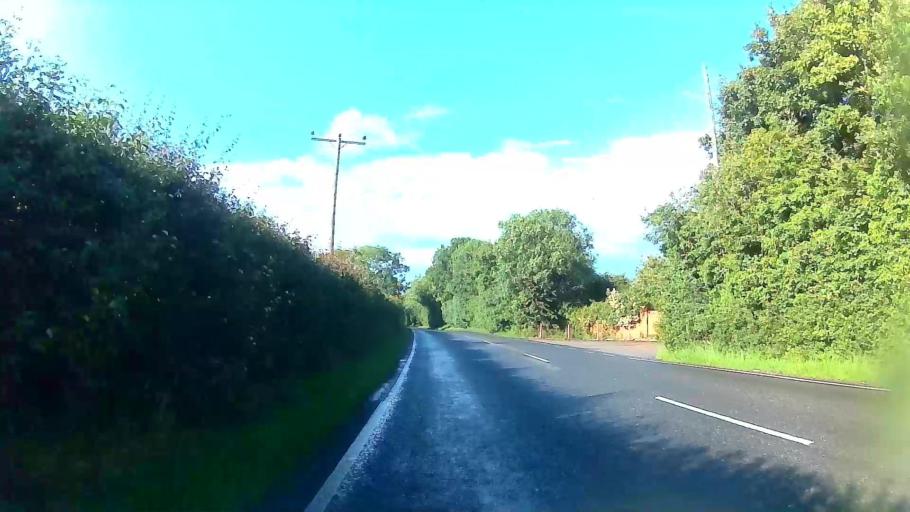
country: GB
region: England
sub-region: Essex
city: Writtle
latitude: 51.7188
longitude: 0.3994
